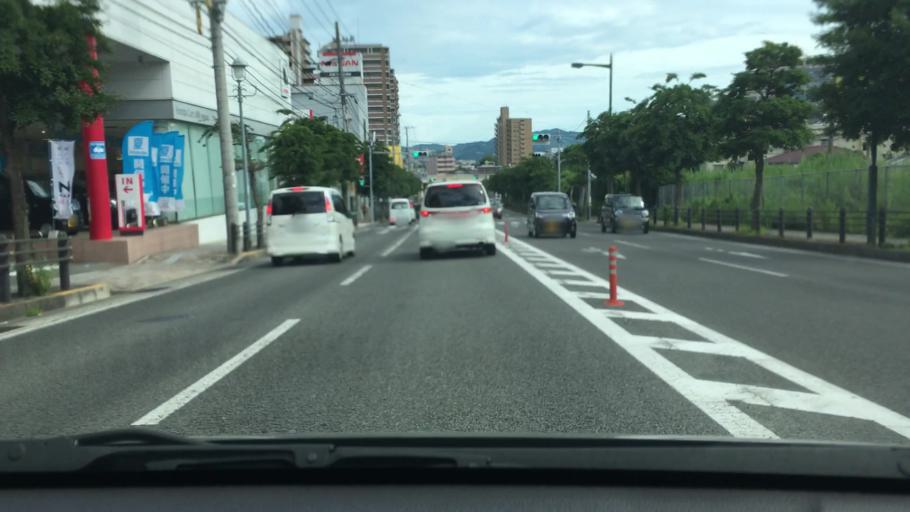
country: JP
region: Nagasaki
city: Togitsu
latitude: 32.7996
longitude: 129.8537
